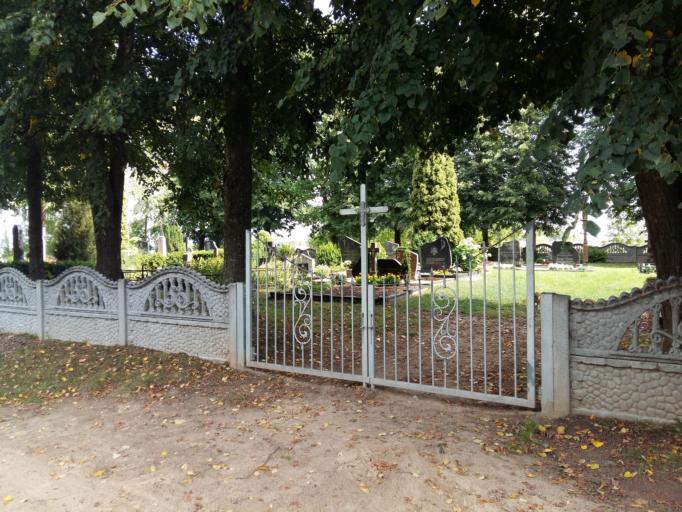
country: LT
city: Ziezmariai
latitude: 54.8138
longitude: 24.2540
